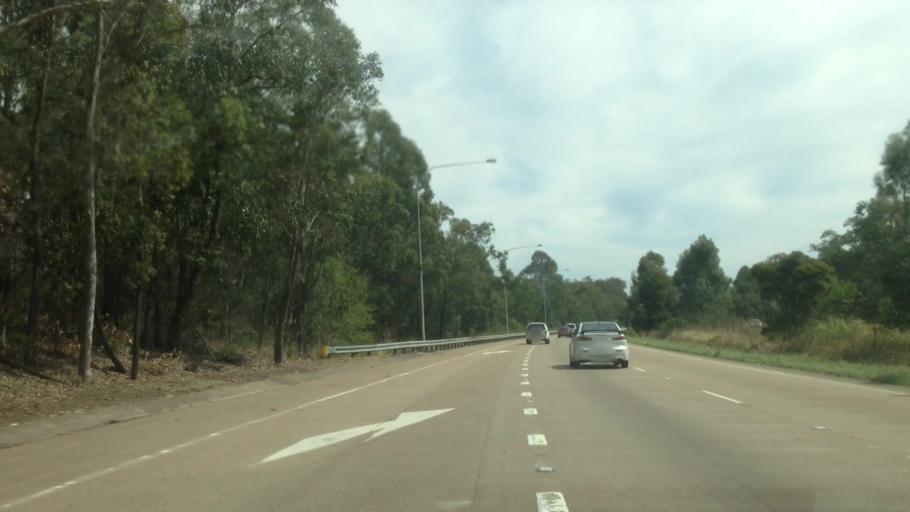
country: AU
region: New South Wales
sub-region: Lake Macquarie Shire
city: Holmesville
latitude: -32.8932
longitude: 151.5957
